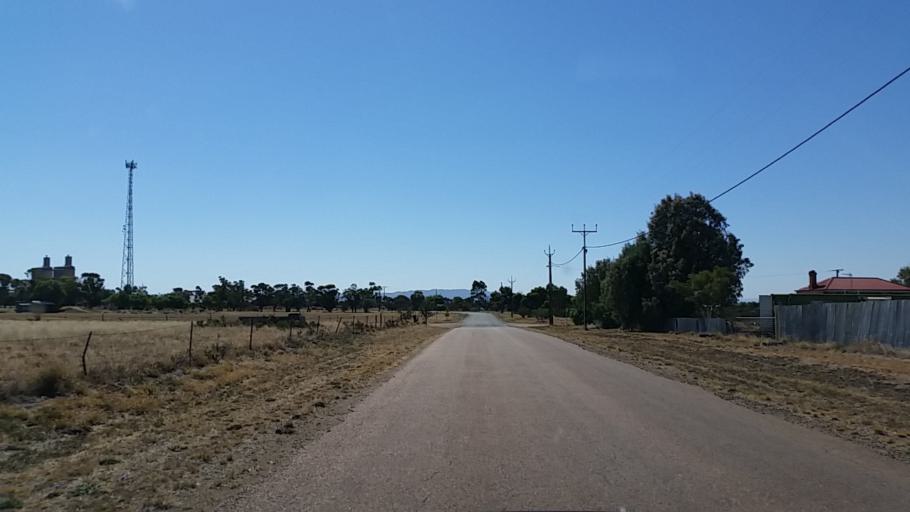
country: AU
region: South Australia
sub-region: Peterborough
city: Peterborough
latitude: -32.7359
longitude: 138.6217
